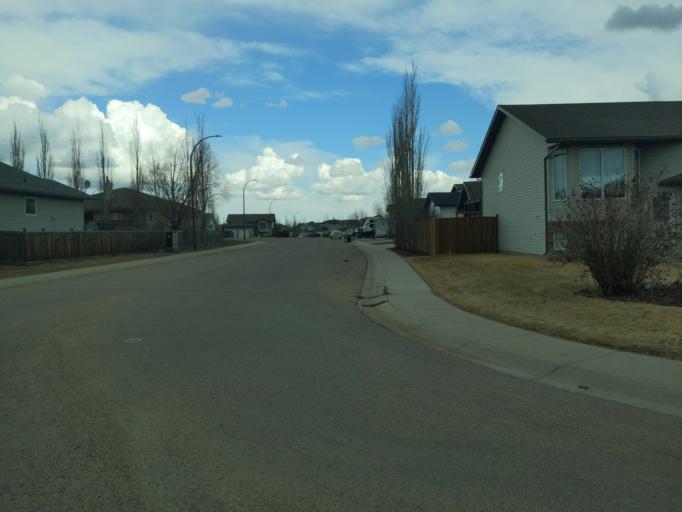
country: CA
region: Saskatchewan
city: Lloydminster
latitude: 53.2663
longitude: -110.0417
